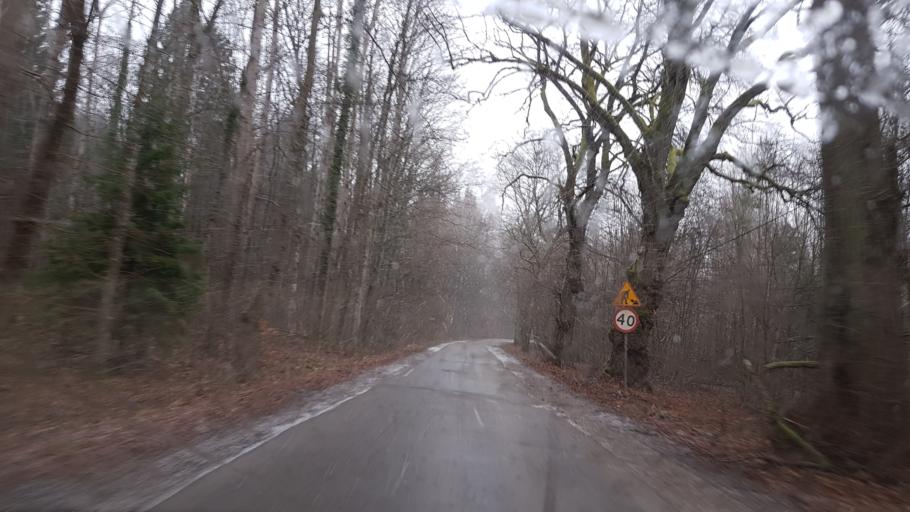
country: PL
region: West Pomeranian Voivodeship
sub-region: Powiat slawienski
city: Slawno
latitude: 54.2556
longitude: 16.5783
